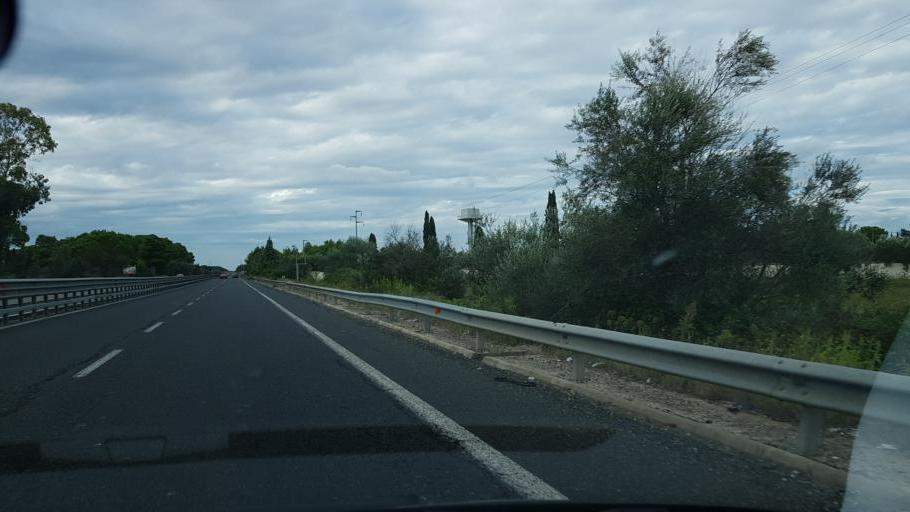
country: IT
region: Apulia
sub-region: Provincia di Lecce
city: San Donato di Lecce
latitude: 40.2832
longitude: 18.2008
